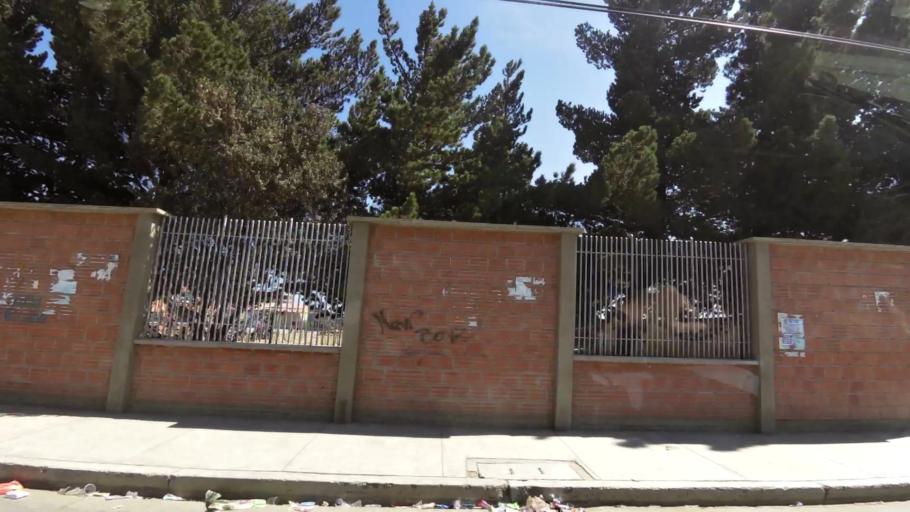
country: BO
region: La Paz
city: La Paz
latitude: -16.5290
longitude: -68.1588
